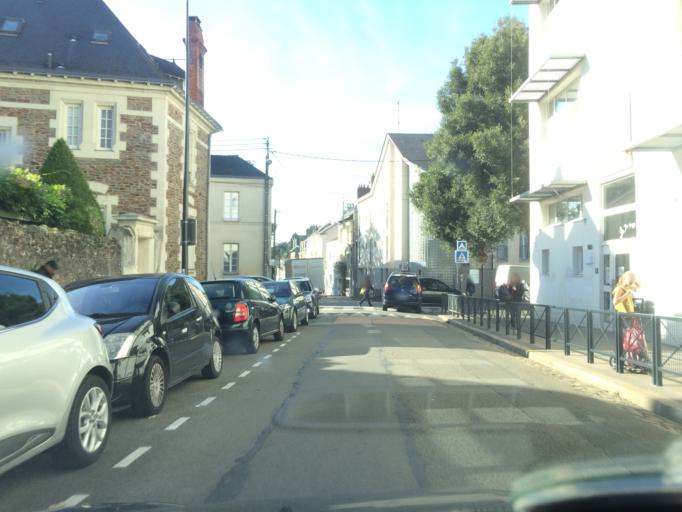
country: FR
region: Pays de la Loire
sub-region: Departement de la Loire-Atlantique
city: Nantes
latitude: 47.2295
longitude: -1.5439
